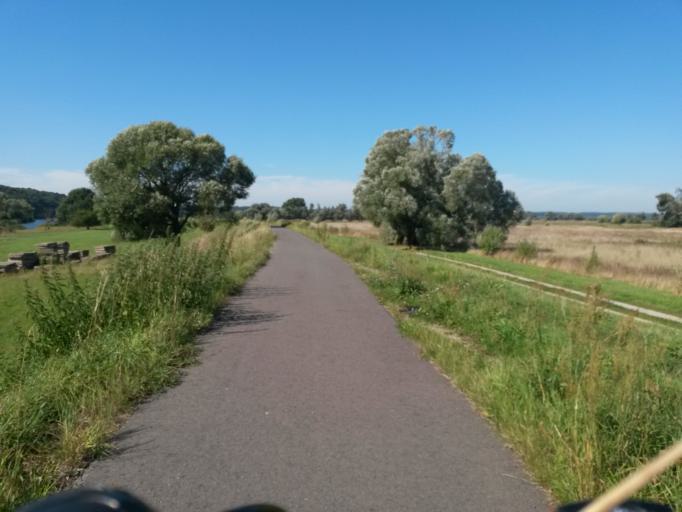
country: DE
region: Brandenburg
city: Schoneberg
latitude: 52.9364
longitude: 14.1267
